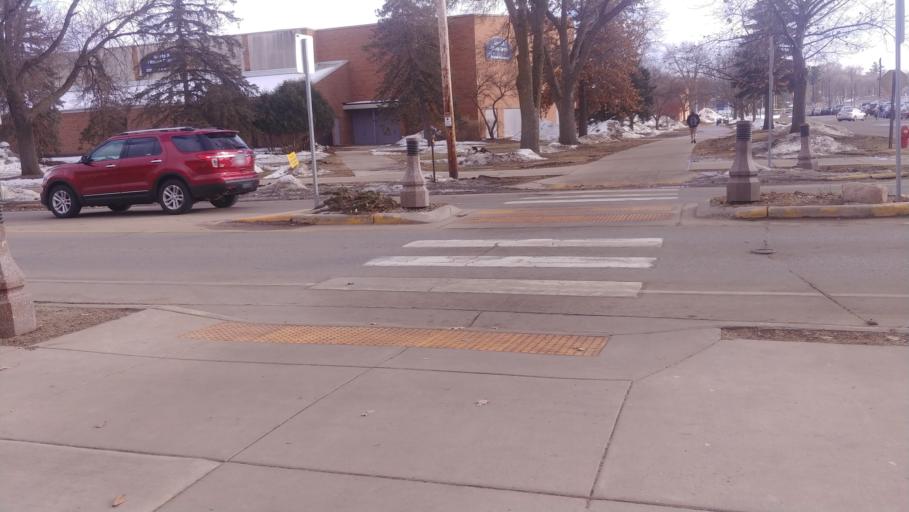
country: US
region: Wisconsin
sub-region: Dunn County
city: Menomonie
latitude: 44.8715
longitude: -91.9284
